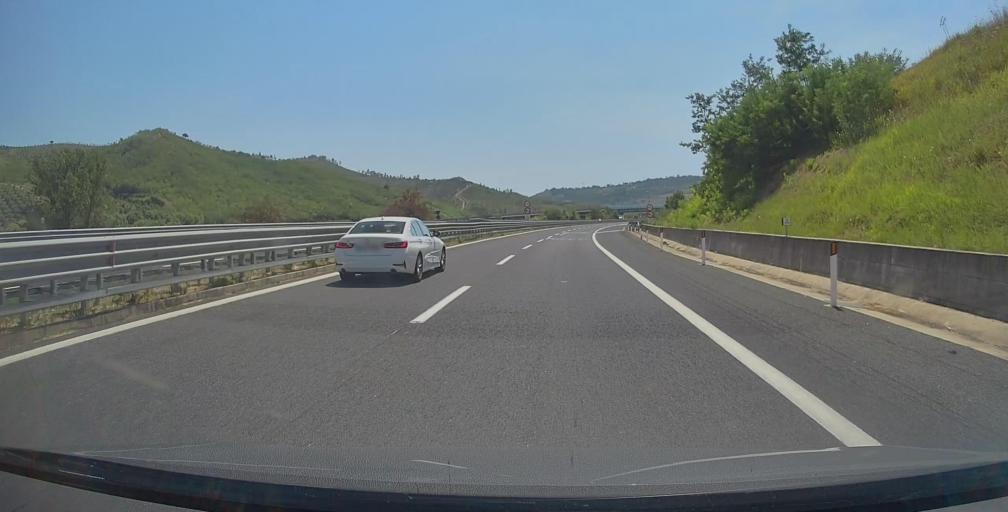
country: IT
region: Calabria
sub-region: Provincia di Vibo-Valentia
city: Paravati
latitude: 38.5670
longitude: 16.0857
